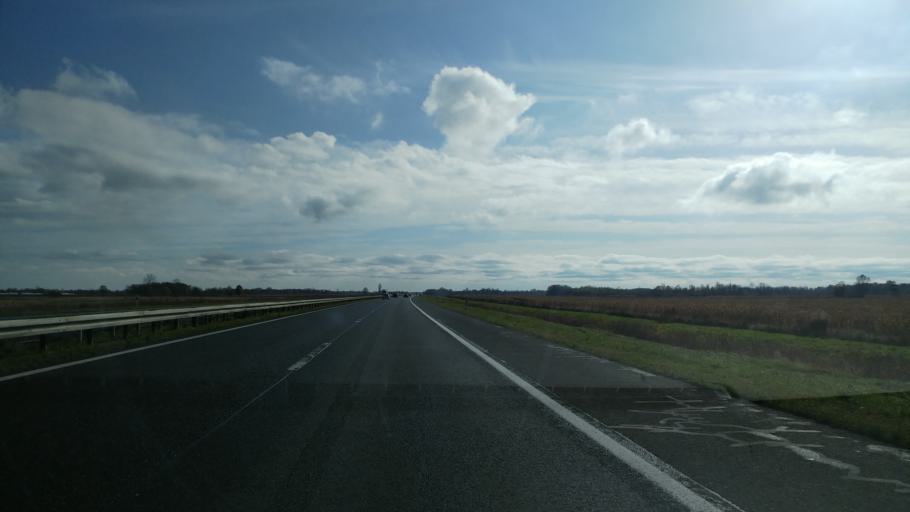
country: HR
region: Zagrebacka
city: Lupoglav
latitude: 45.7328
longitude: 16.3361
